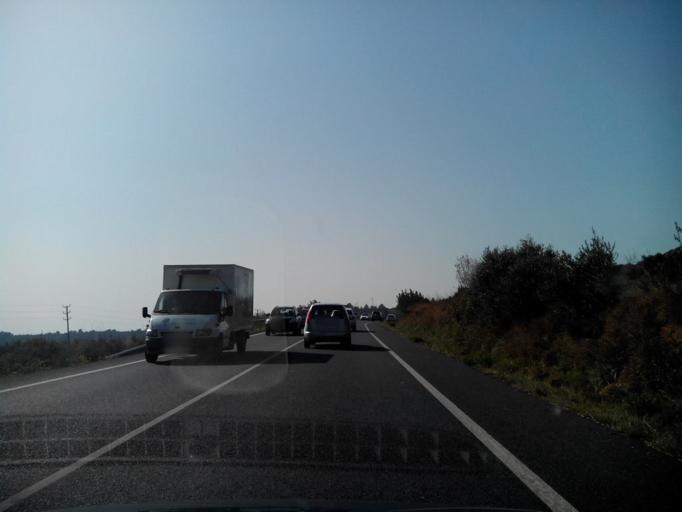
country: ES
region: Catalonia
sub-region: Provincia de Tarragona
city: Alcover
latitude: 41.2964
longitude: 1.1921
